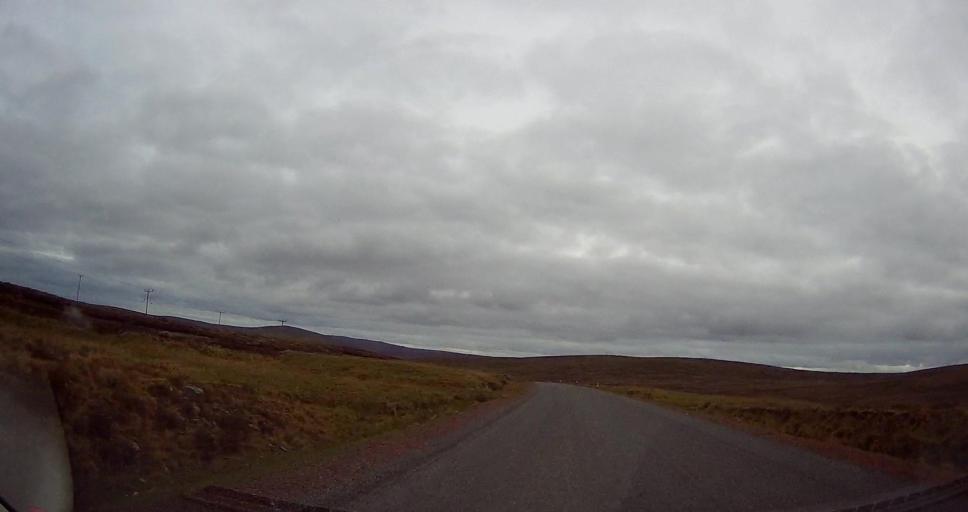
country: GB
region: Scotland
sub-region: Shetland Islands
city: Shetland
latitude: 60.6266
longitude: -1.0714
